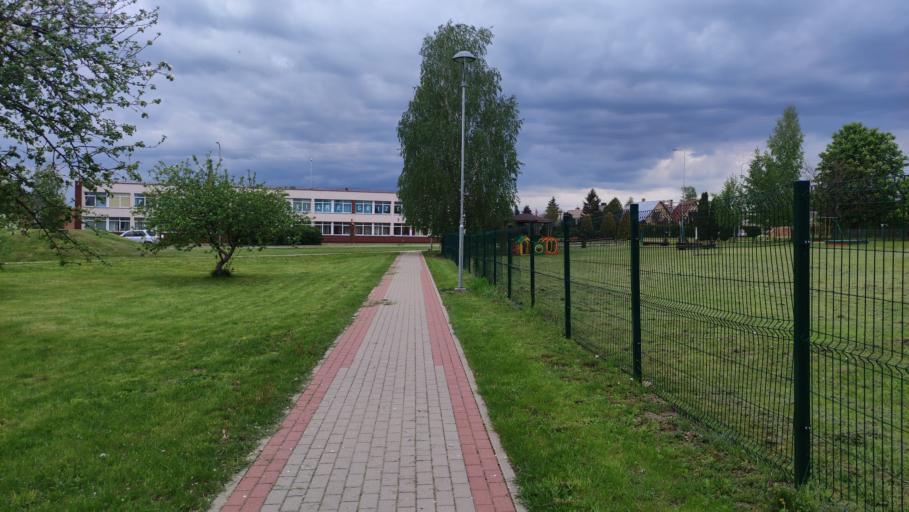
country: LT
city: Jieznas
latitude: 54.5028
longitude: 24.2509
